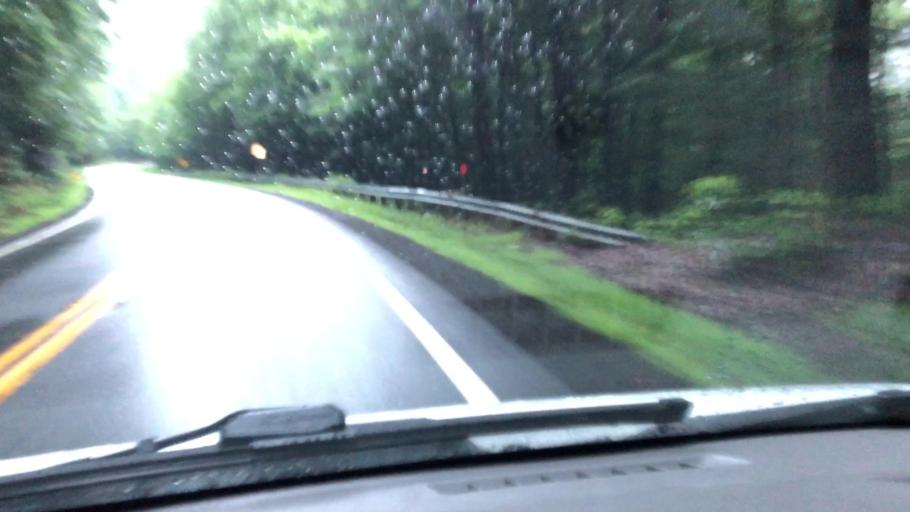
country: US
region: Massachusetts
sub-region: Hampshire County
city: Westhampton
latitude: 42.2928
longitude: -72.8705
